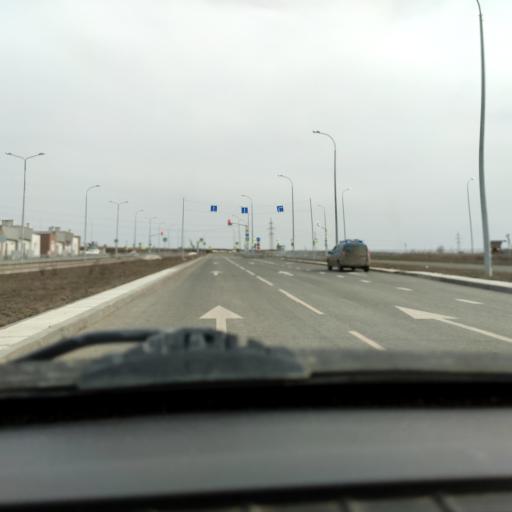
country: RU
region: Samara
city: Petra-Dubrava
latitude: 53.2928
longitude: 50.3311
